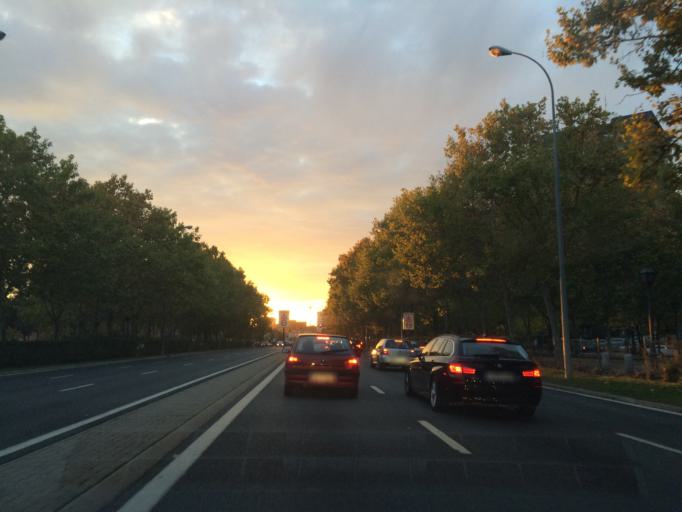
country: ES
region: Madrid
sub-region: Provincia de Madrid
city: Tetuan de las Victorias
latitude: 40.4816
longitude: -3.7072
